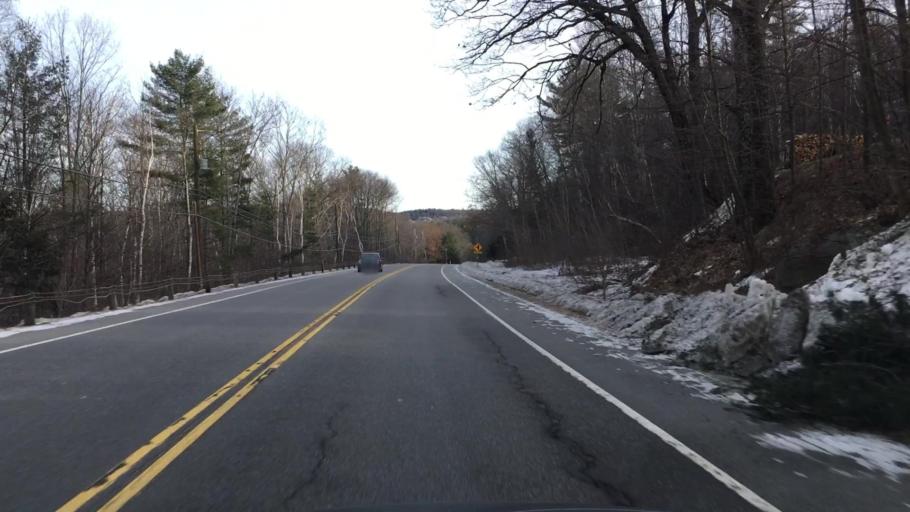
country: US
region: New Hampshire
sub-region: Sullivan County
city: Sunapee
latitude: 43.3436
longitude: -72.0871
